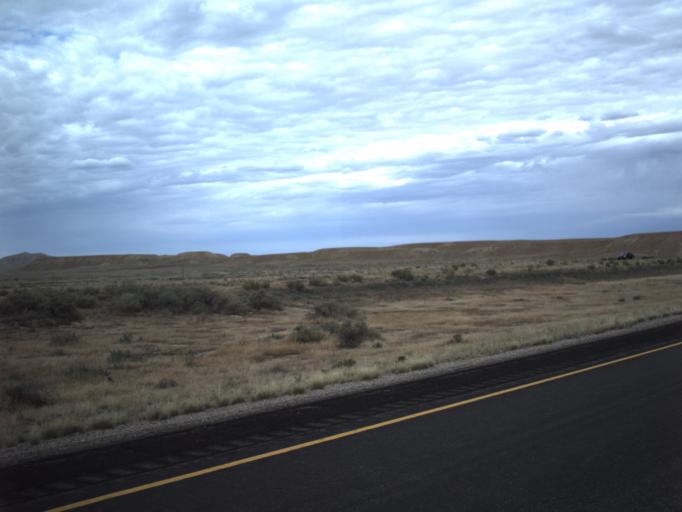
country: US
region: Utah
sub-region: Grand County
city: Moab
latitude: 38.9437
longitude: -109.6422
